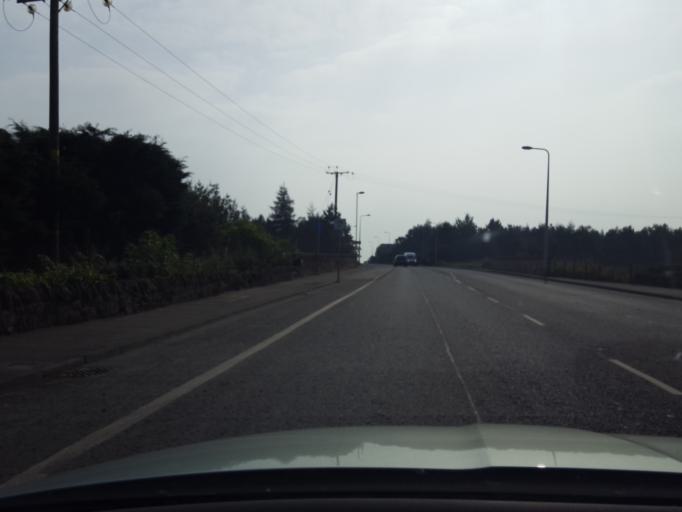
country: GB
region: Scotland
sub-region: Fife
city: Crossgates
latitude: 56.0913
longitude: -3.3721
